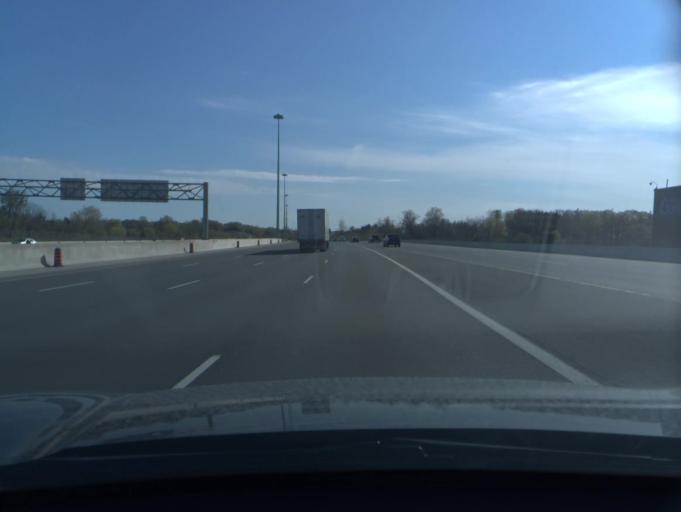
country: CA
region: Ontario
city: North Perth
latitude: 43.8128
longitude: -81.0005
